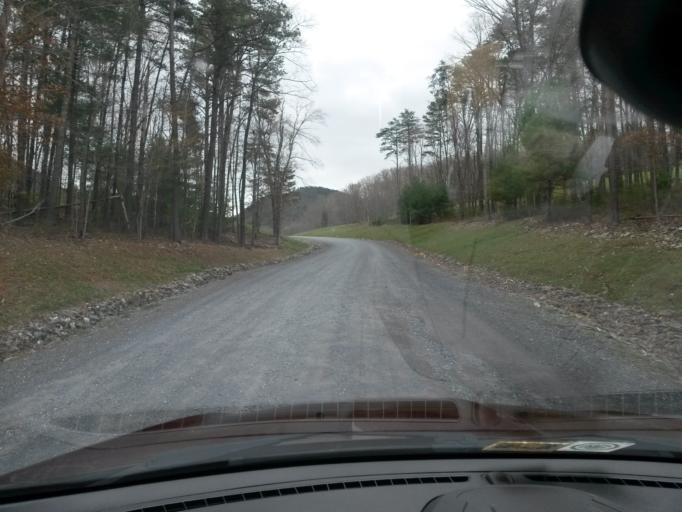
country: US
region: Virginia
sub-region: City of Buena Vista
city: Buena Vista
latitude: 37.7442
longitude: -79.3418
